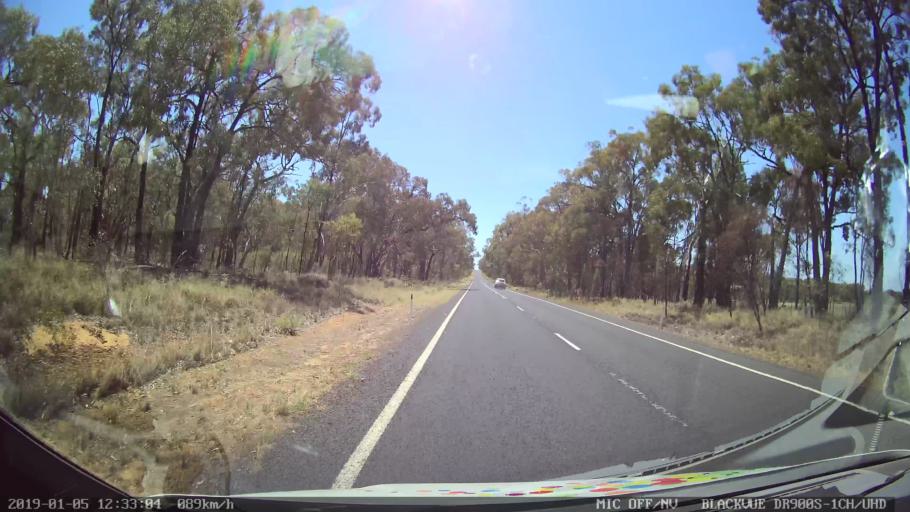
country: AU
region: New South Wales
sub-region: Warrumbungle Shire
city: Coonabarabran
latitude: -31.2156
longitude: 149.3893
